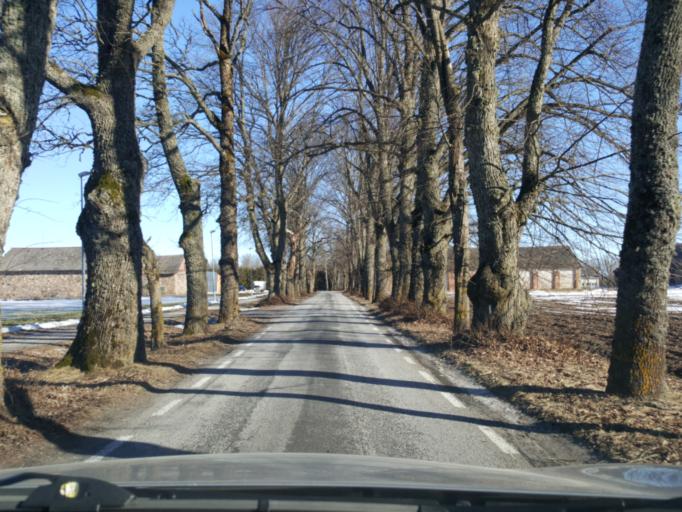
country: EE
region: Viljandimaa
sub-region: Vohma linn
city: Vohma
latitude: 58.5509
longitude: 25.5575
